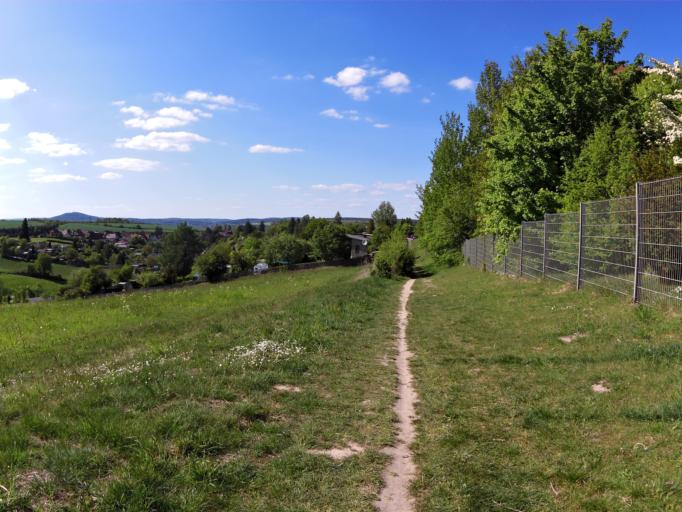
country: DE
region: Thuringia
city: Leimbach
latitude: 50.8028
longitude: 10.2169
